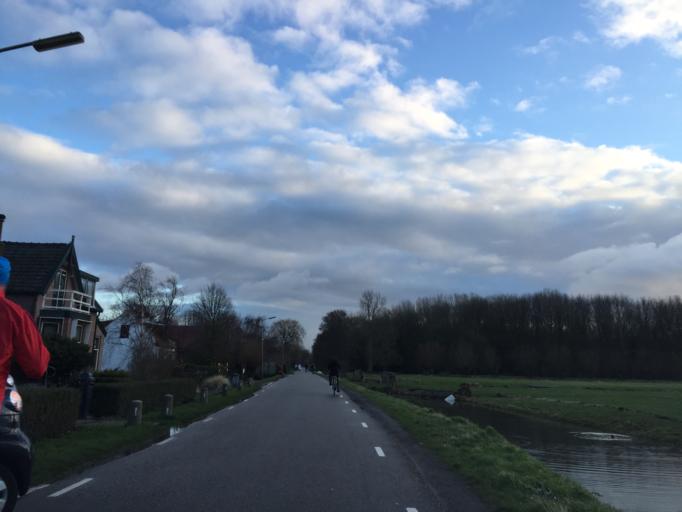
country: NL
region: South Holland
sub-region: Gemeente Den Haag
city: Ypenburg
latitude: 52.0182
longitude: 4.3900
